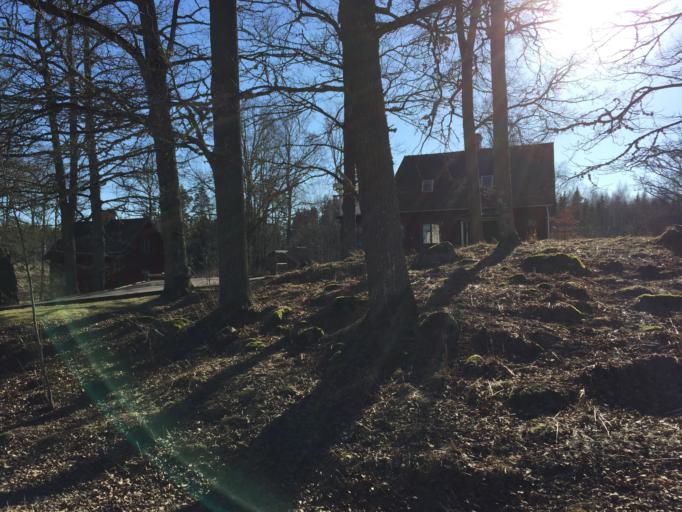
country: SE
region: Soedermanland
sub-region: Vingakers Kommun
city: Vingaker
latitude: 58.9147
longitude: 15.8750
